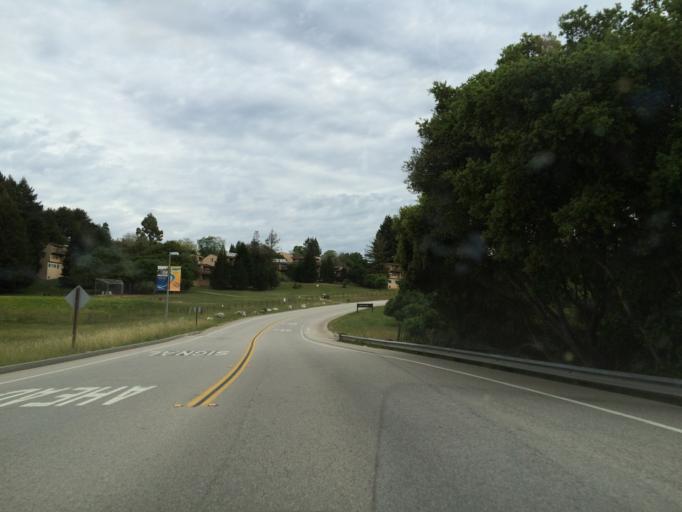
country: US
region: California
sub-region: Santa Cruz County
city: Santa Cruz
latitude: 36.9883
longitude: -122.0682
